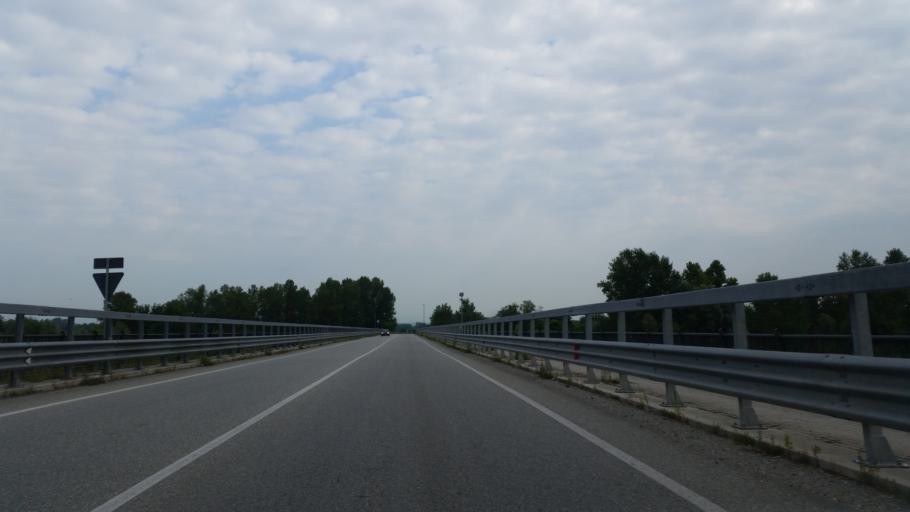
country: IT
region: Piedmont
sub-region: Provincia di Torino
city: San Sebastiano da Po
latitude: 45.1718
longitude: 7.9427
